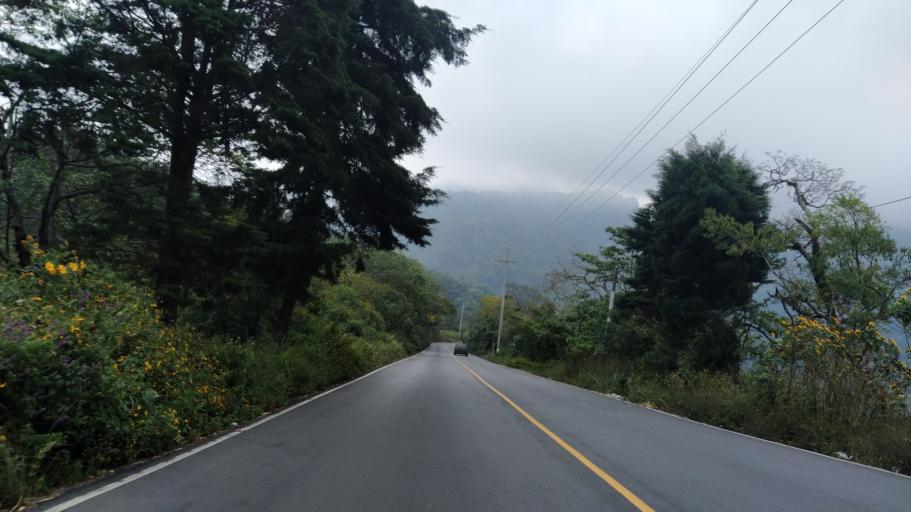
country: GT
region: Quetzaltenango
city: Zunil
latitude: 14.7326
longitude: -91.5229
